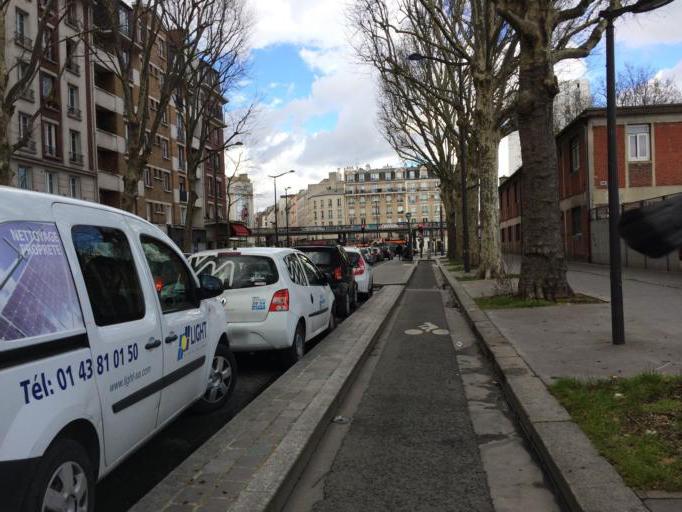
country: FR
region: Ile-de-France
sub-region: Departement du Val-de-Marne
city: Ivry-sur-Seine
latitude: 48.8241
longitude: 2.3782
